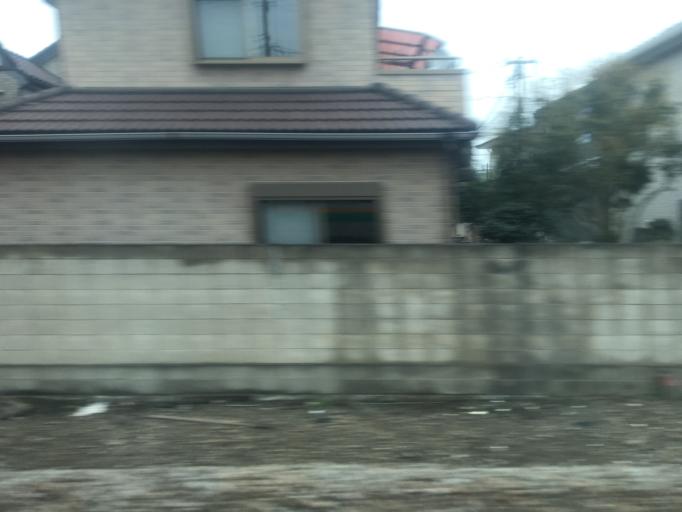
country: JP
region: Saitama
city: Okegawa
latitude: 35.9934
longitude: 139.5699
